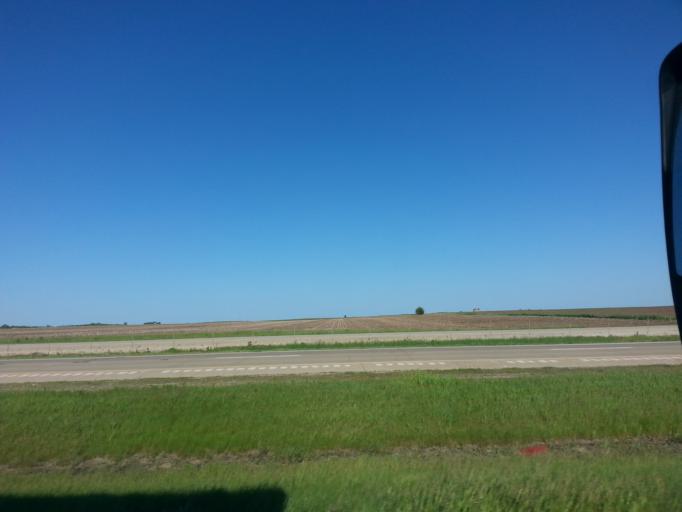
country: US
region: Illinois
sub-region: Marshall County
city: Wenona
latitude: 41.0871
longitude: -89.0674
